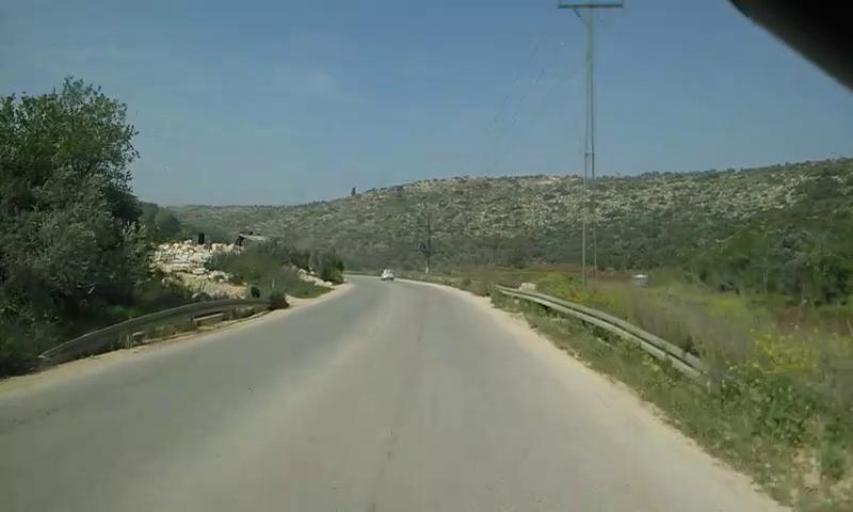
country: PS
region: West Bank
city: Az Zababidah
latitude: 32.4069
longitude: 35.3102
